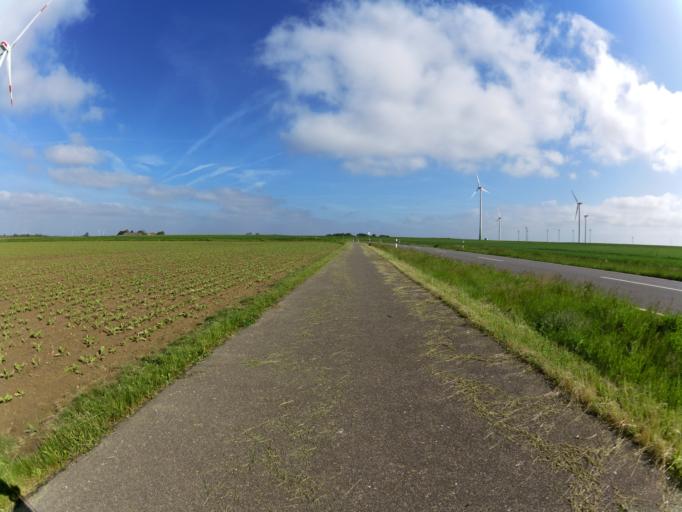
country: DE
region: North Rhine-Westphalia
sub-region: Regierungsbezirk Koln
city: Linnich
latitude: 50.9757
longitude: 6.2168
